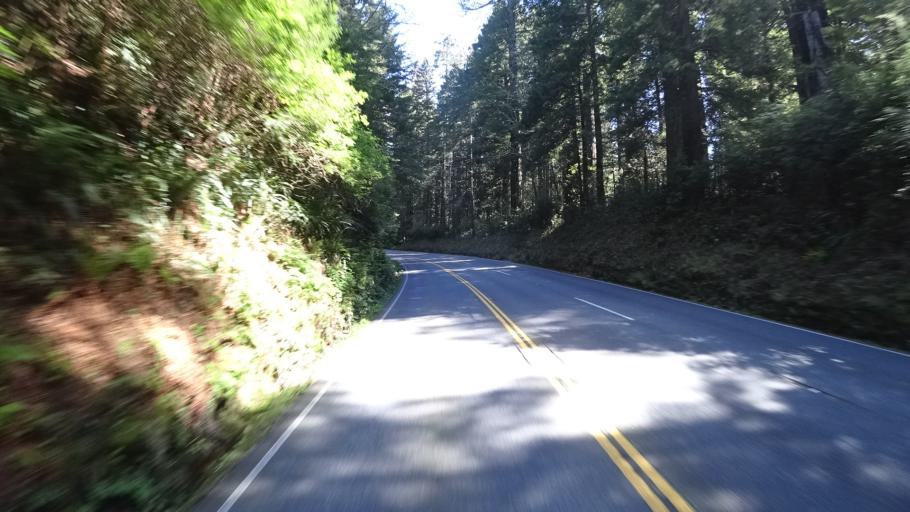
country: US
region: California
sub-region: Del Norte County
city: Bertsch-Oceanview
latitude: 41.6461
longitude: -124.1125
